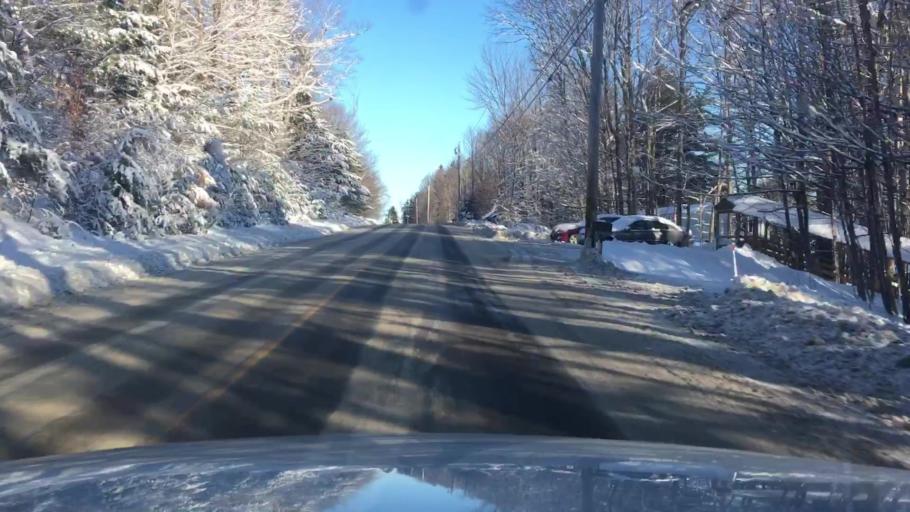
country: US
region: Maine
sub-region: Kennebec County
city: Mount Vernon
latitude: 44.4523
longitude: -69.9705
